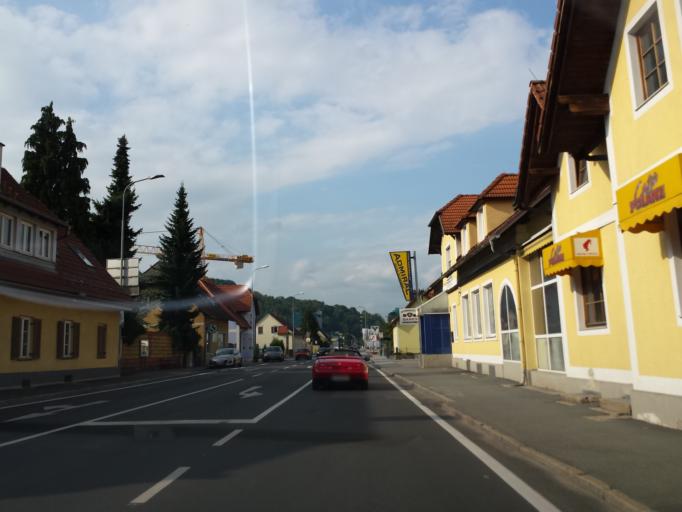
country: AT
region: Styria
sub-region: Politischer Bezirk Graz-Umgebung
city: Seiersberg
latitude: 47.0101
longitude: 15.3990
